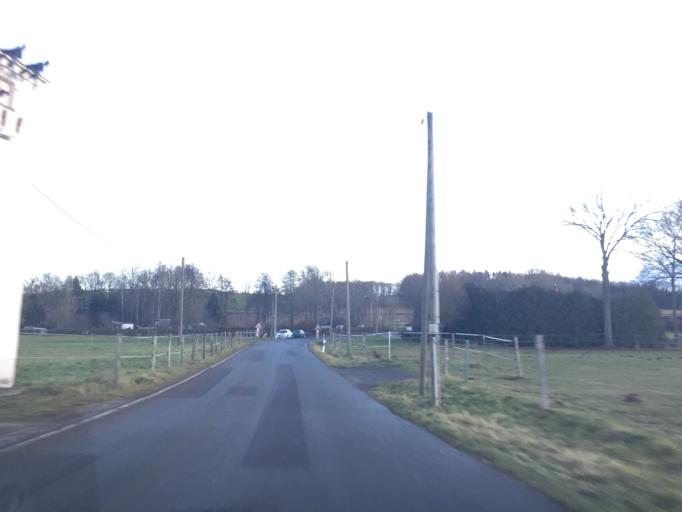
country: DE
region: Thuringia
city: Nobdenitz
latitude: 50.8860
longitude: 12.3057
